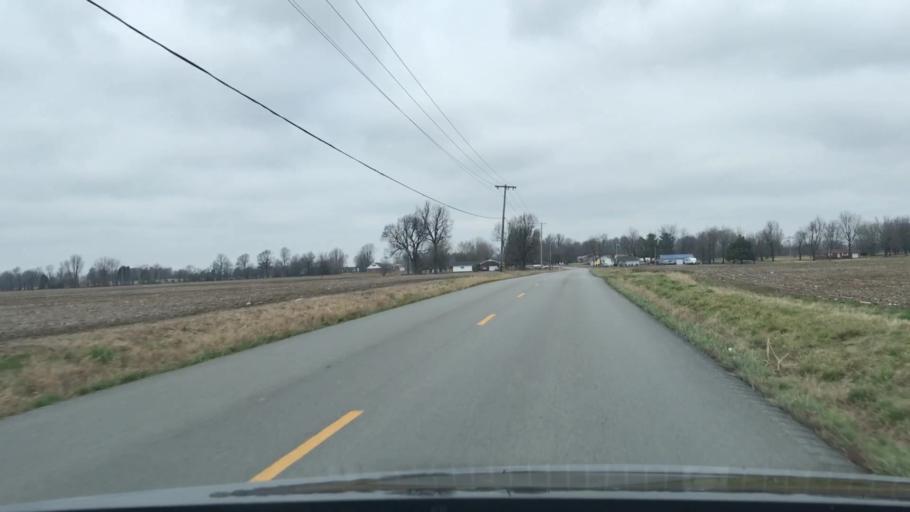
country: US
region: Kentucky
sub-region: Muhlenberg County
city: Morehead
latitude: 37.3534
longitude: -87.2281
